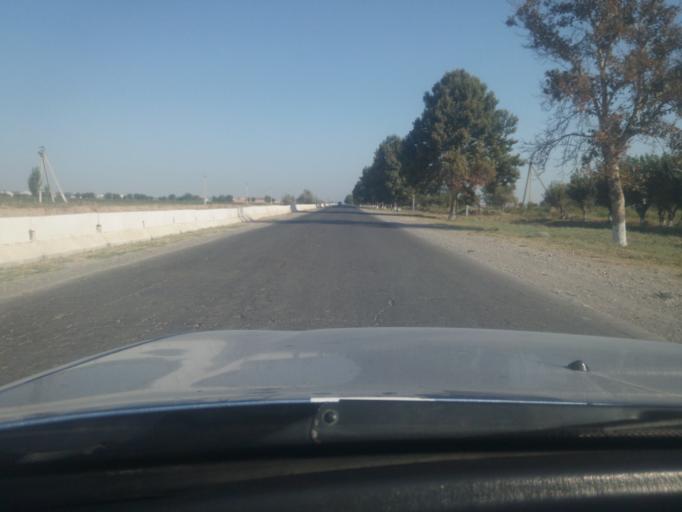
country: UZ
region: Sirdaryo
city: Guliston
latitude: 40.5010
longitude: 68.7983
